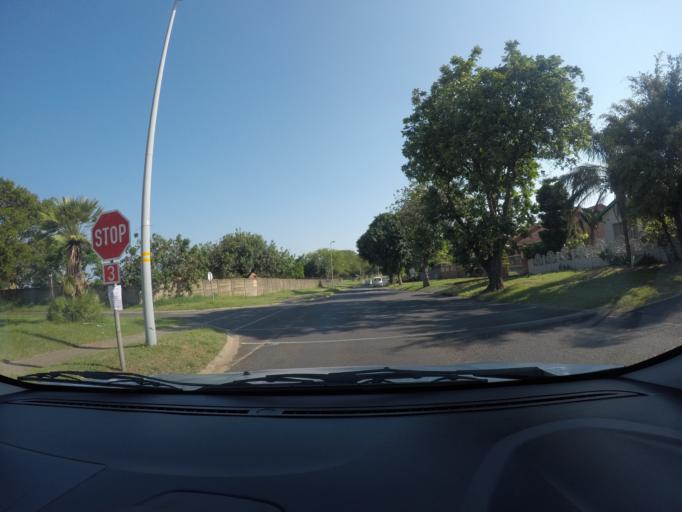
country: ZA
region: KwaZulu-Natal
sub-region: uThungulu District Municipality
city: Richards Bay
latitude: -28.7259
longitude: 32.0419
